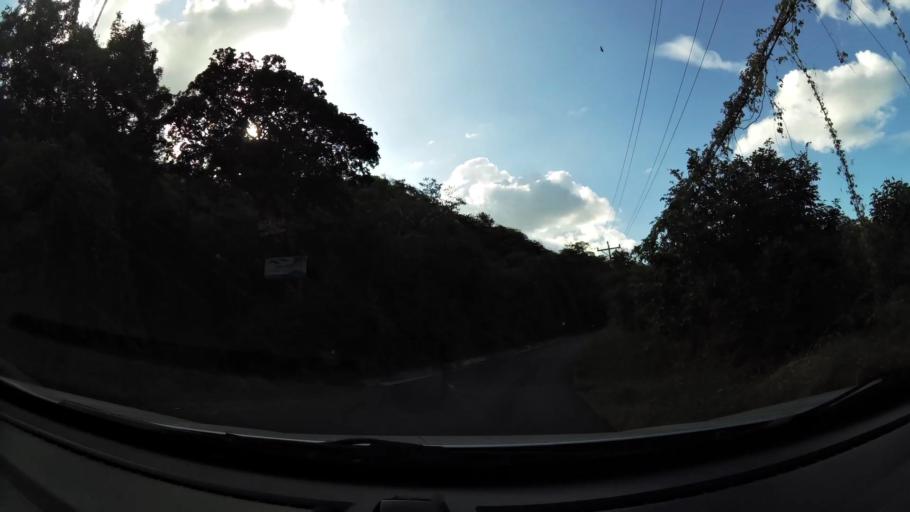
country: CR
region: Guanacaste
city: Sardinal
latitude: 10.5652
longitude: -85.6789
